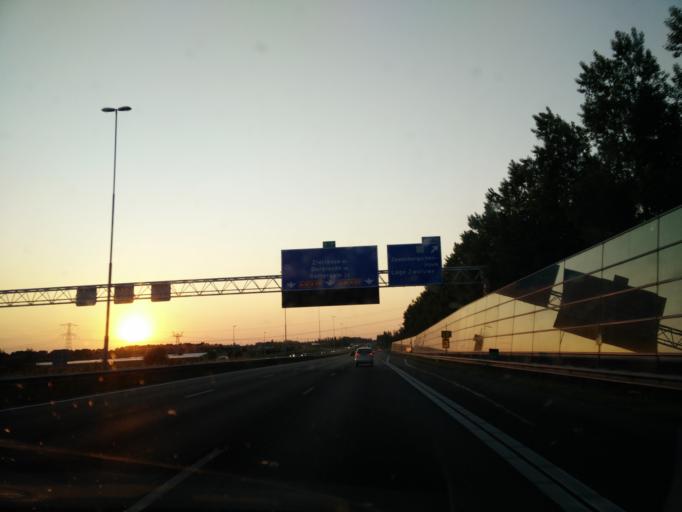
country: NL
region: North Brabant
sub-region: Gemeente Made en Drimmelen
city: Made
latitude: 51.6773
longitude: 4.6684
